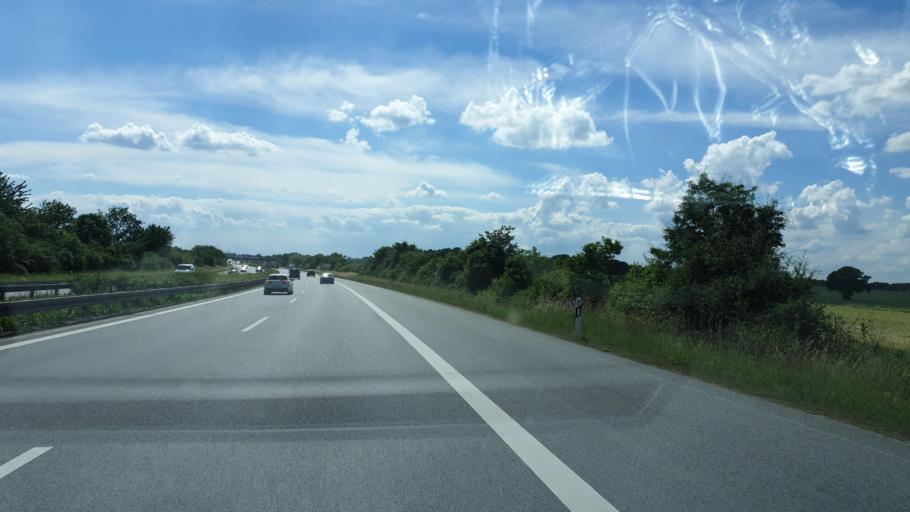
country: DE
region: Saxony
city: Malschwitz
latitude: 51.2055
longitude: 14.4890
